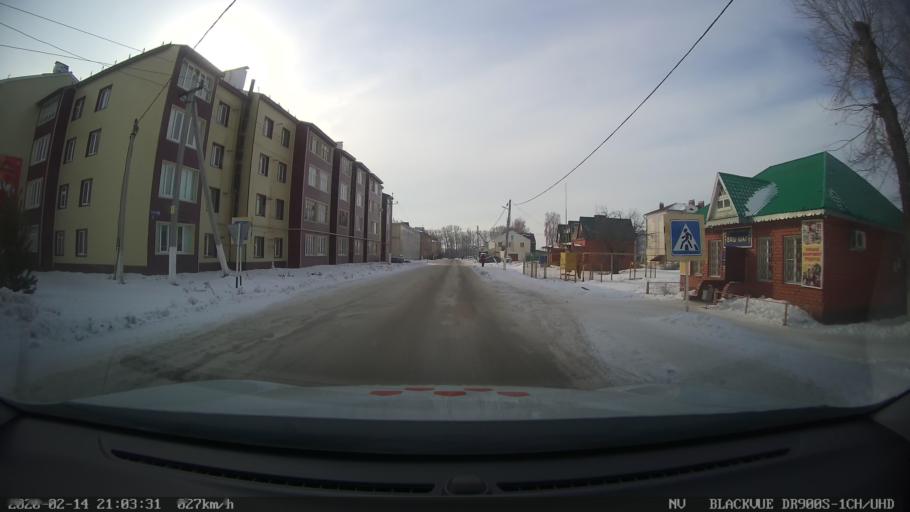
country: RU
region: Tatarstan
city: Kuybyshevskiy Zaton
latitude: 55.1564
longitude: 49.1756
